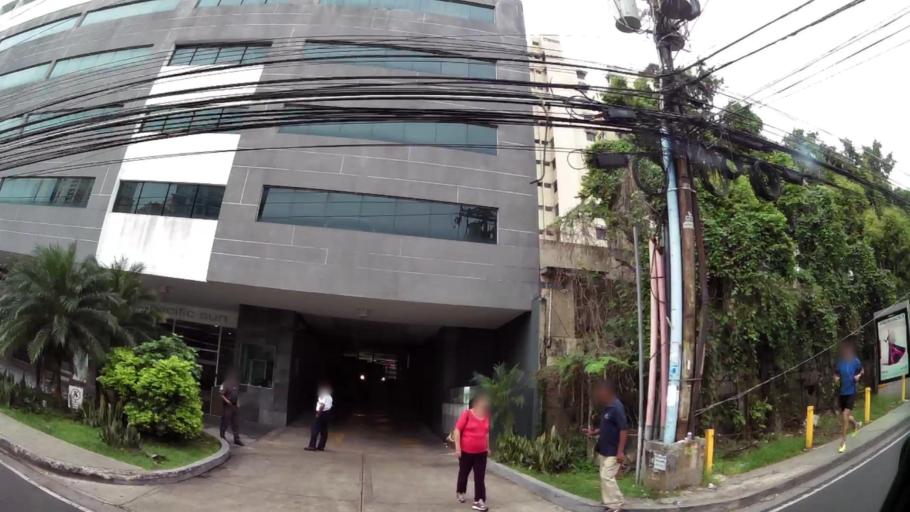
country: PA
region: Panama
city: Panama
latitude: 8.9777
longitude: -79.5130
